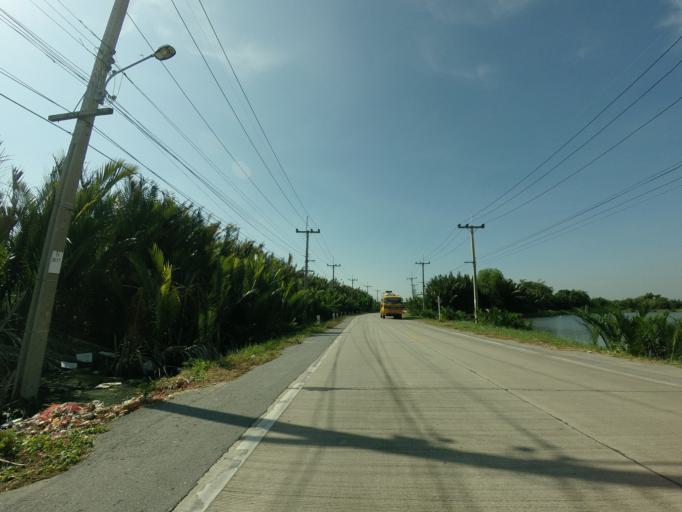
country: TH
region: Samut Prakan
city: Phra Samut Chedi
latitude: 13.5581
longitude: 100.5385
